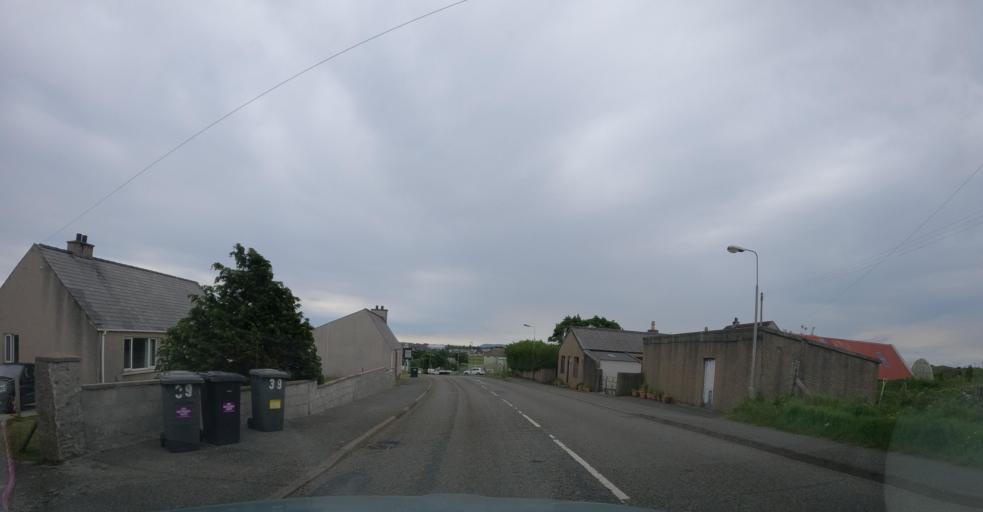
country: GB
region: Scotland
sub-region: Eilean Siar
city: Isle of Lewis
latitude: 58.2310
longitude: -6.3901
